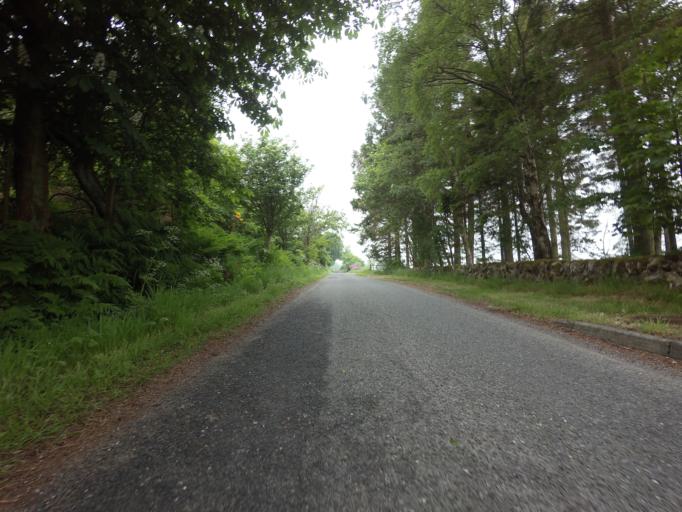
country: GB
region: Scotland
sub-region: Perth and Kinross
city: Kinross
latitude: 56.1620
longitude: -3.4504
